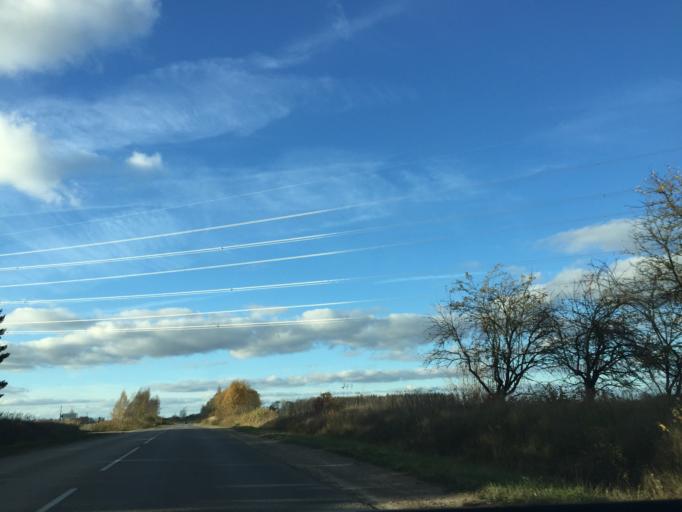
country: LV
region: Tukuma Rajons
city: Tukums
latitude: 56.9824
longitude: 23.1113
